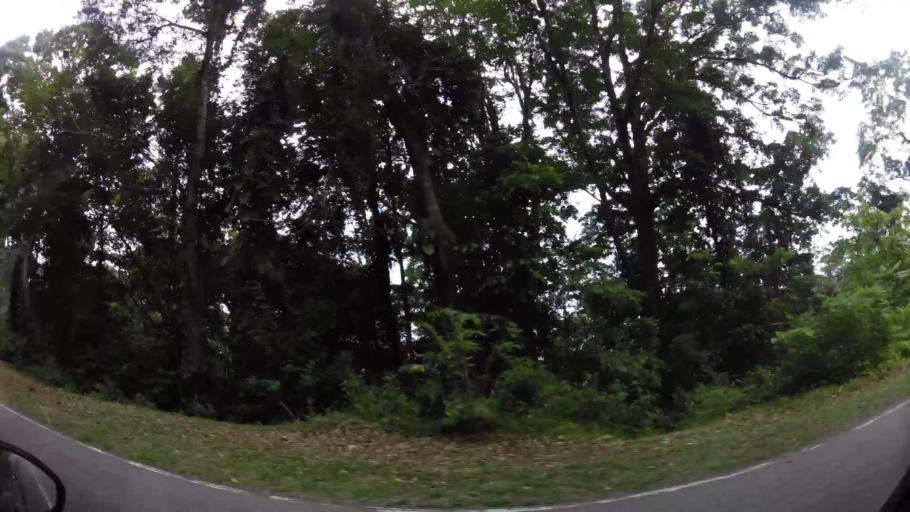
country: TT
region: Diego Martin
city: Petit Valley
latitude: 10.7395
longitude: -61.4936
